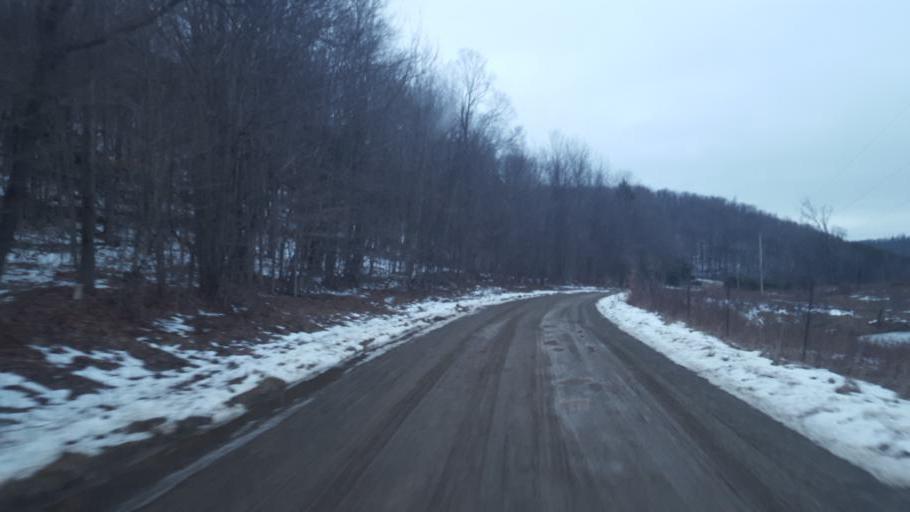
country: US
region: Pennsylvania
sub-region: Potter County
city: Coudersport
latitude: 41.8908
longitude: -77.8308
